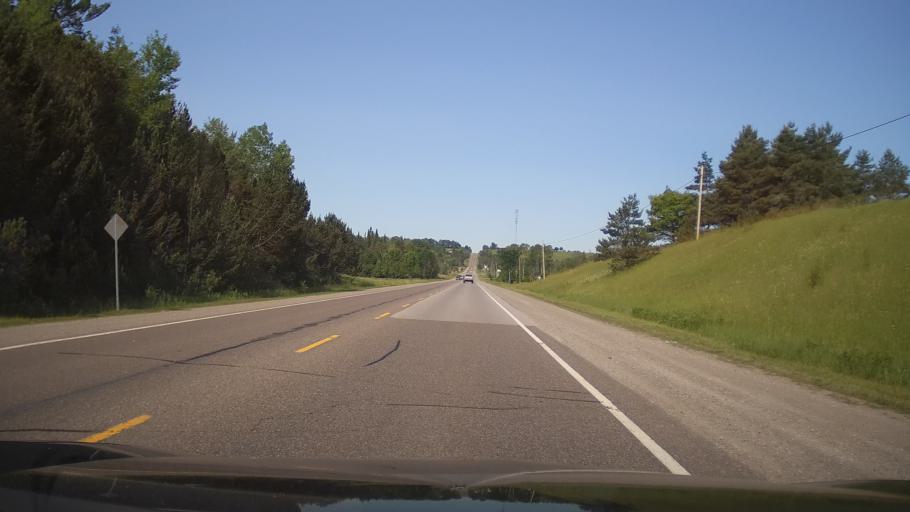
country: CA
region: Ontario
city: Omemee
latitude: 44.3216
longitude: -78.4675
